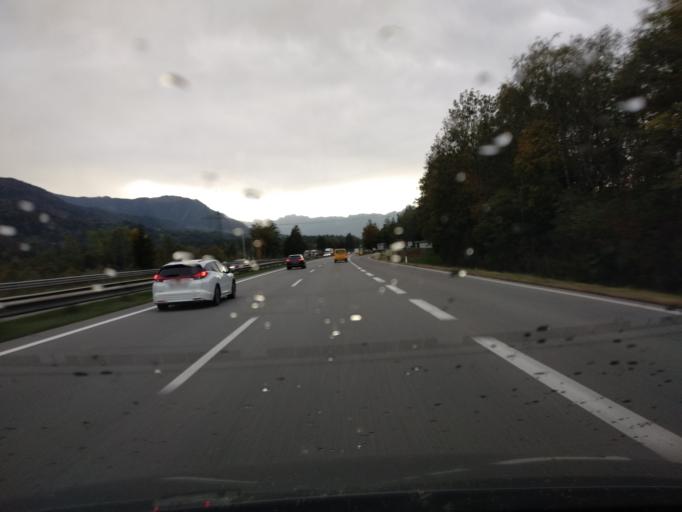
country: AT
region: Vorarlberg
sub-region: Politischer Bezirk Feldkirch
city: Schlins
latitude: 47.2003
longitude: 9.6816
